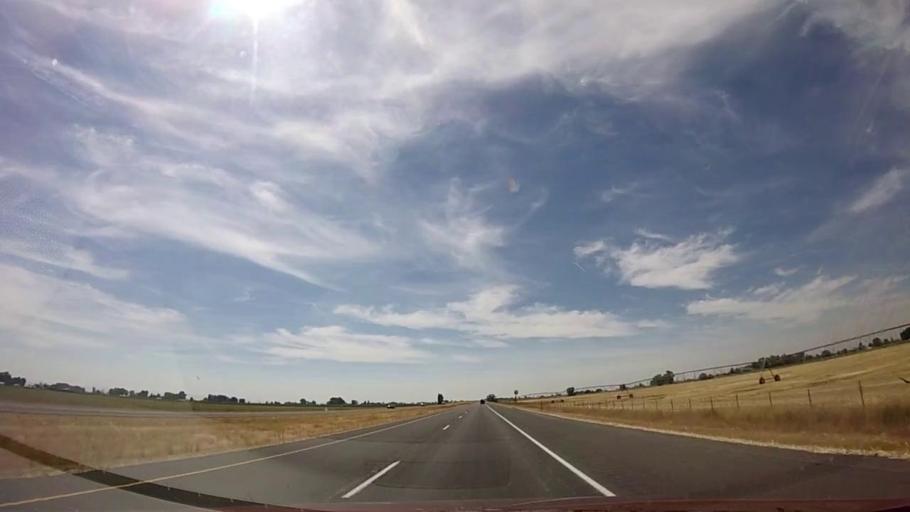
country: US
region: Idaho
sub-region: Minidoka County
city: Rupert
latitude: 42.5690
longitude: -113.6522
